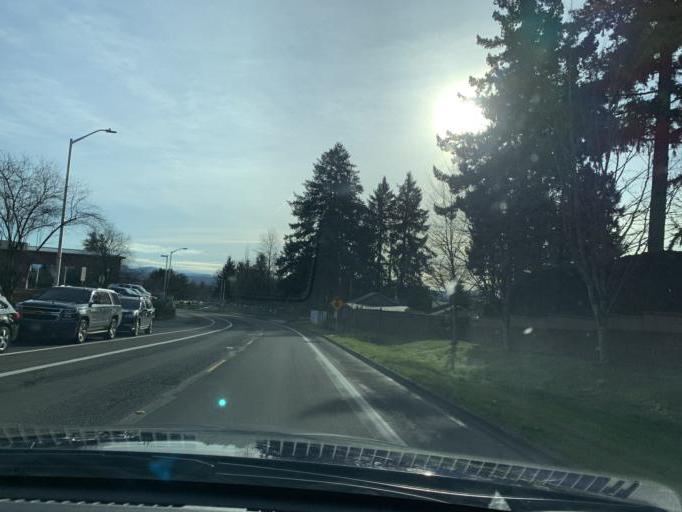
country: US
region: Washington
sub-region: Clark County
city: Mill Plain
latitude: 45.5977
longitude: -122.5059
